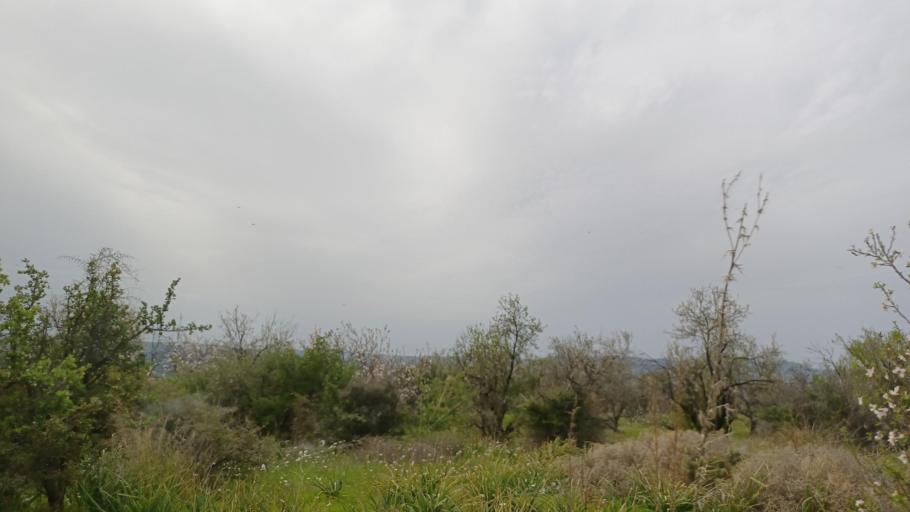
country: CY
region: Pafos
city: Polis
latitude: 35.0437
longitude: 32.4761
